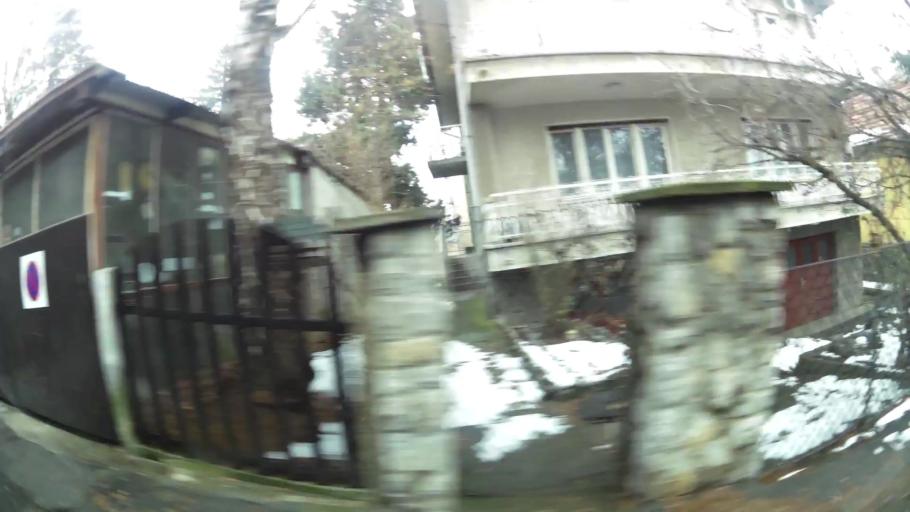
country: RS
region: Central Serbia
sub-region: Belgrade
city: Vozdovac
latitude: 44.7740
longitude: 20.4788
